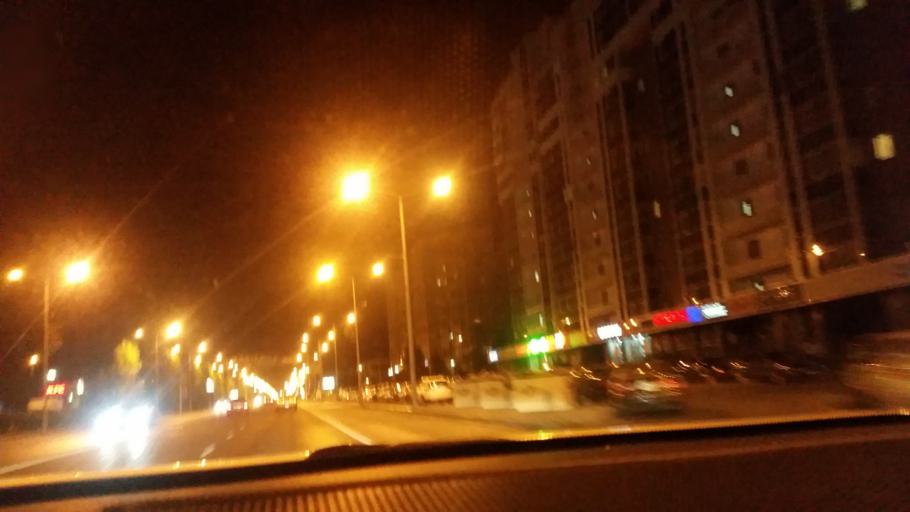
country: KZ
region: Astana Qalasy
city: Astana
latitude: 51.1412
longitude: 71.4828
